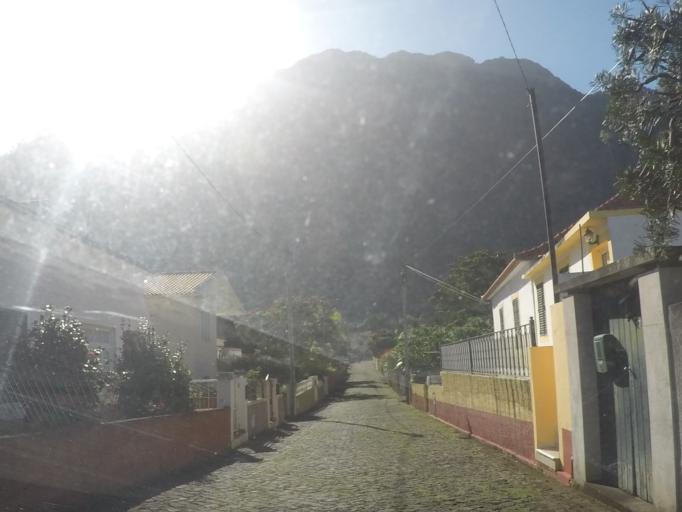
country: PT
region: Madeira
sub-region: Santana
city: Santana
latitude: 32.8284
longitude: -16.9543
